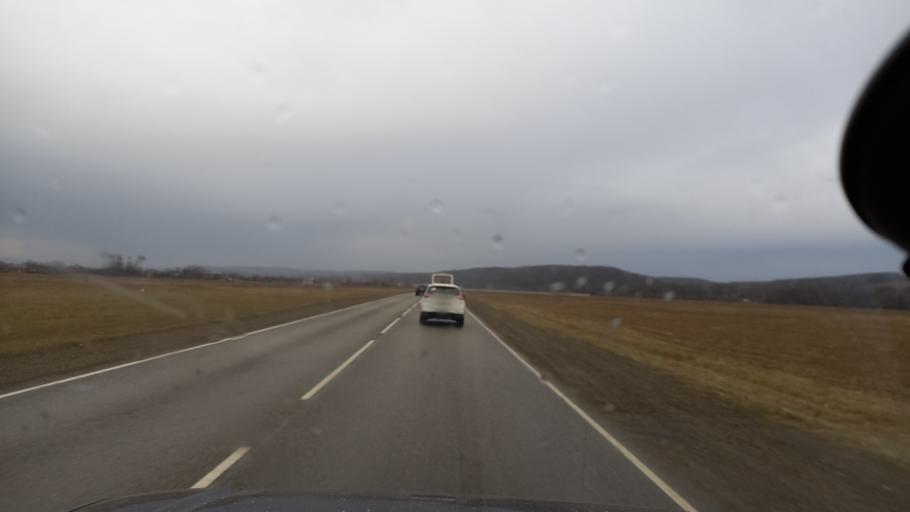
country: RU
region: Adygeya
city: Tul'skiy
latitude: 44.5365
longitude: 40.1400
